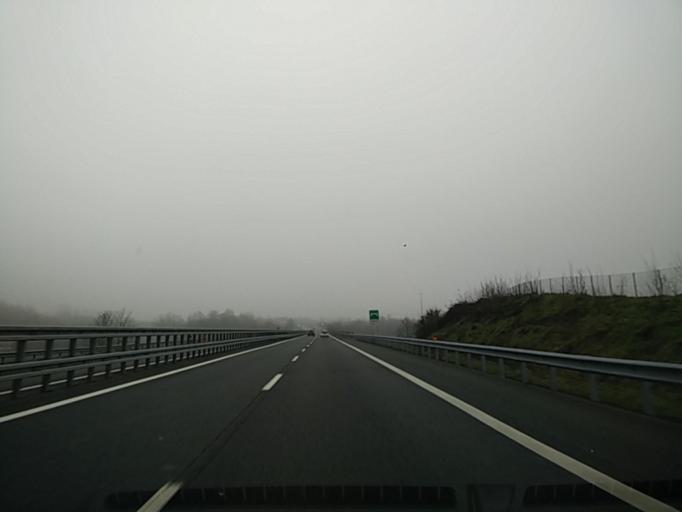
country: IT
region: Piedmont
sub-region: Provincia di Asti
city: Baldichieri d'Asti
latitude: 44.9029
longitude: 8.1139
